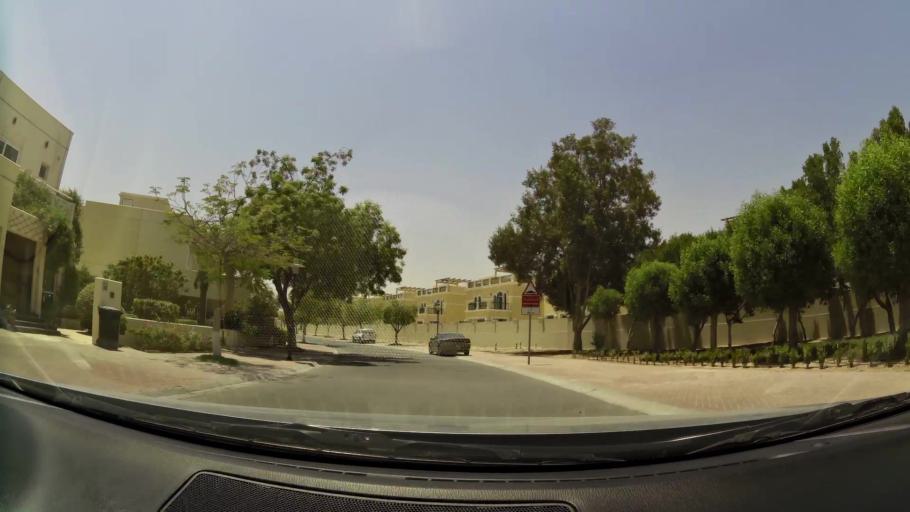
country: AE
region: Dubai
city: Dubai
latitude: 25.0437
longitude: 55.1701
